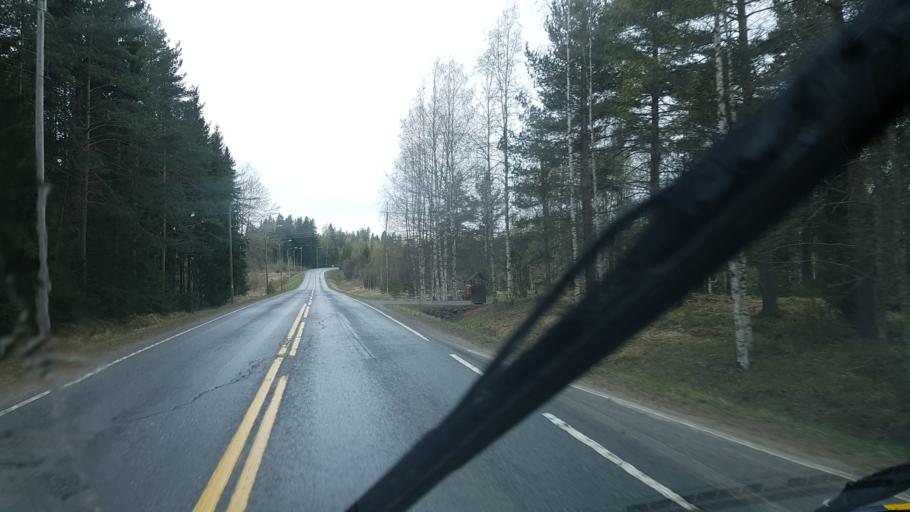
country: FI
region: Pirkanmaa
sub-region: Tampere
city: Pirkkala
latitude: 61.4286
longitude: 23.6290
